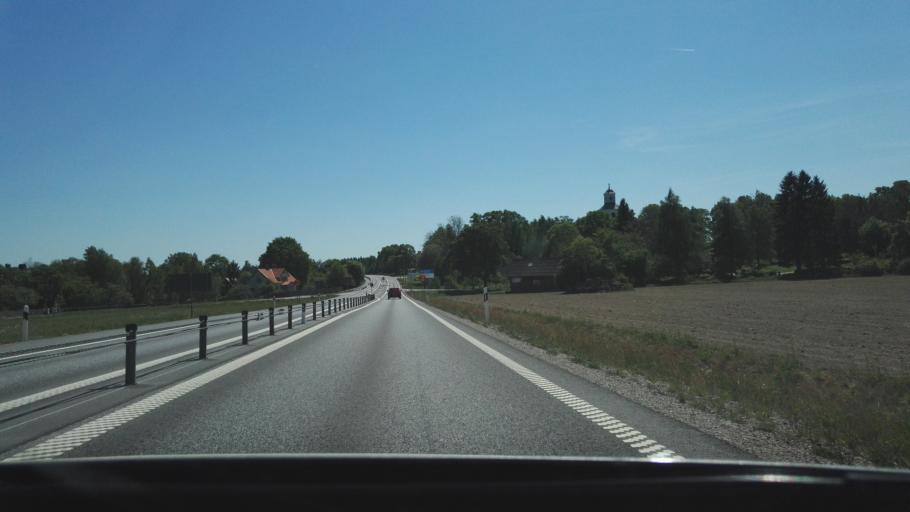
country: SE
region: Kronoberg
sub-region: Vaxjo Kommun
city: Ingelstad
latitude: 56.6501
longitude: 14.9160
